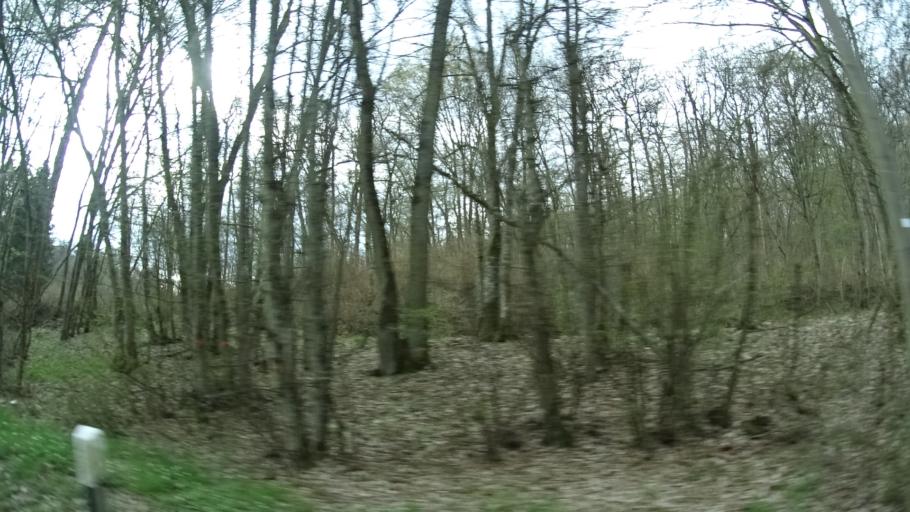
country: DE
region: Rheinland-Pfalz
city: Allenfeld
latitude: 49.8528
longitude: 7.6588
